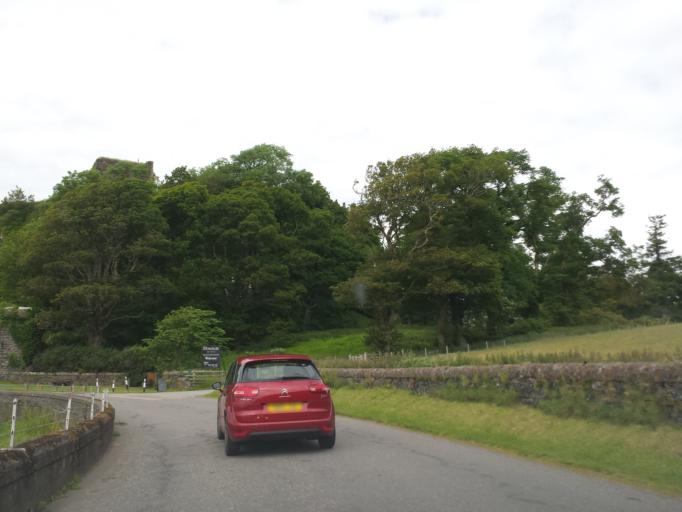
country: GB
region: Scotland
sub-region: Argyll and Bute
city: Oban
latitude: 56.4254
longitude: -5.4834
